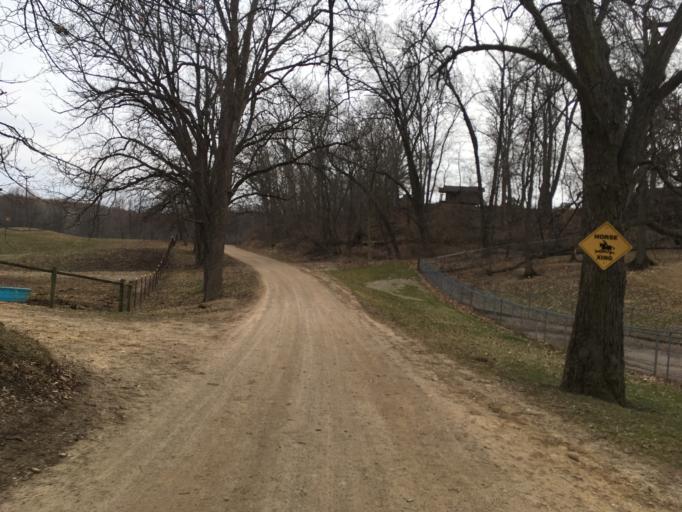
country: US
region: Michigan
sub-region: Jackson County
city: Grass Lake
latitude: 42.3150
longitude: -84.1997
